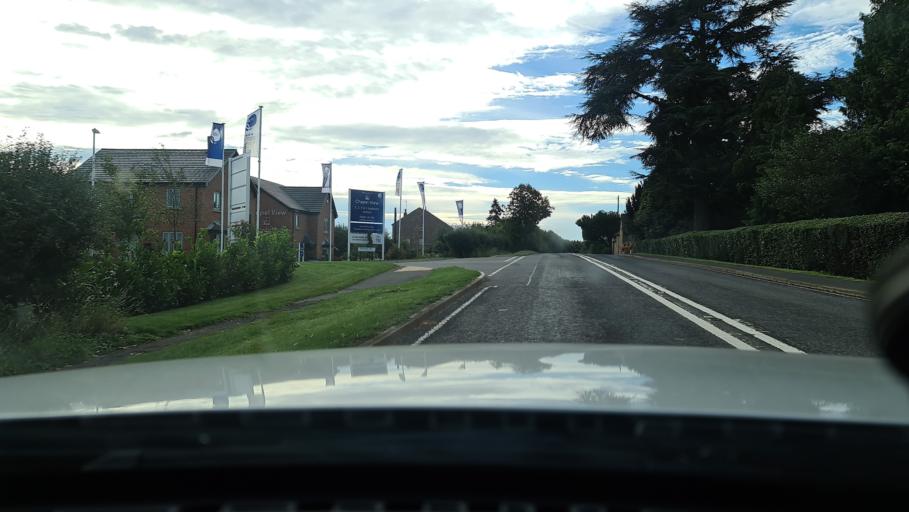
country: GB
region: England
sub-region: Warwickshire
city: Shipston on Stour
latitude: 52.0541
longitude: -1.6222
